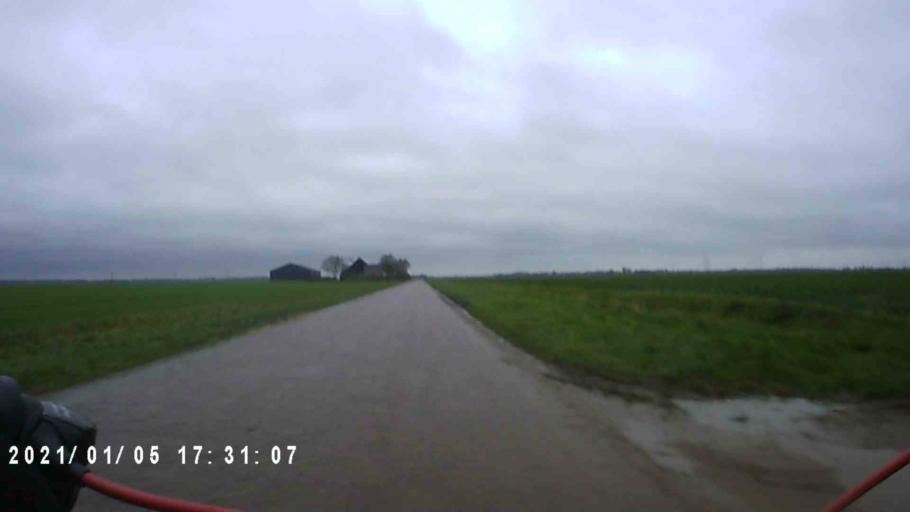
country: NL
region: Groningen
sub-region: Gemeente Delfzijl
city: Delfzijl
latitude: 53.2206
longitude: 6.9370
